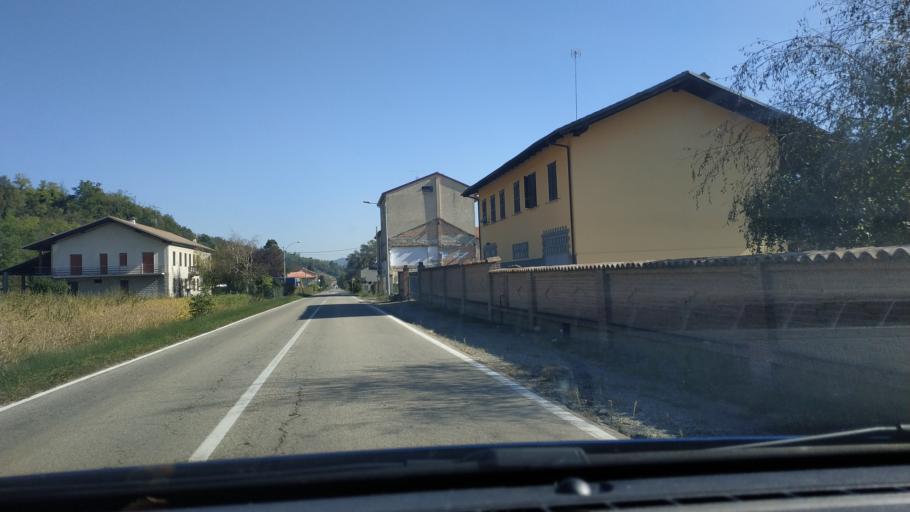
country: IT
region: Piedmont
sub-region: Provincia di Alessandria
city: Cerrina
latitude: 45.1032
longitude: 8.1967
